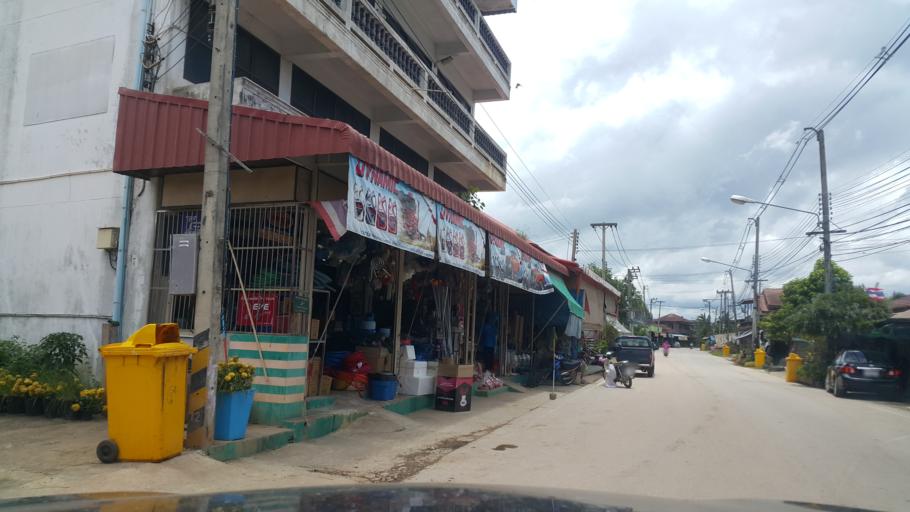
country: TH
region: Sukhothai
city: Kong Krailat
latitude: 16.9325
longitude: 99.9579
